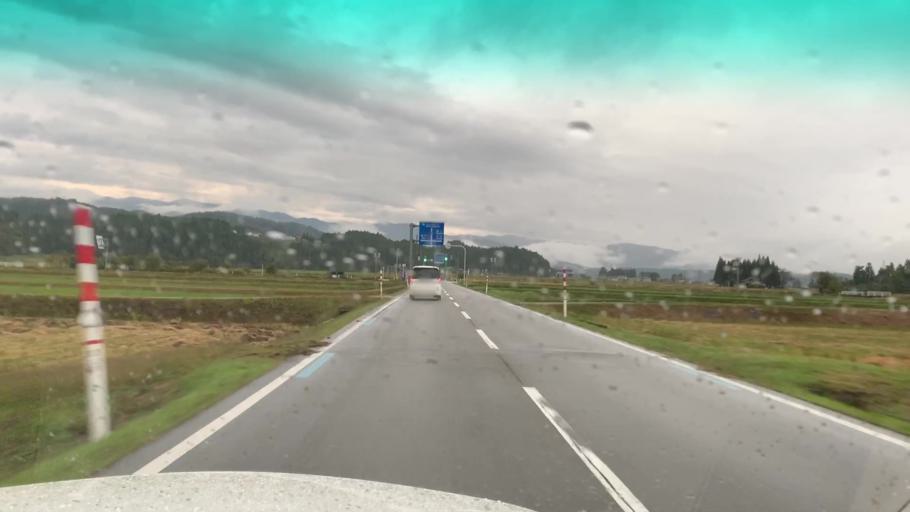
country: JP
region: Toyama
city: Kamiichi
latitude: 36.6273
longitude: 137.3286
